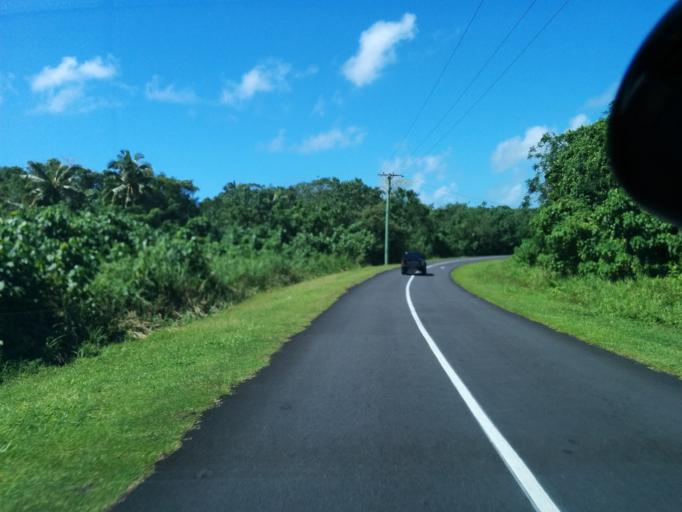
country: WS
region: Fa`asaleleaga
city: Safotulafai
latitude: -13.5503
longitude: -172.2387
